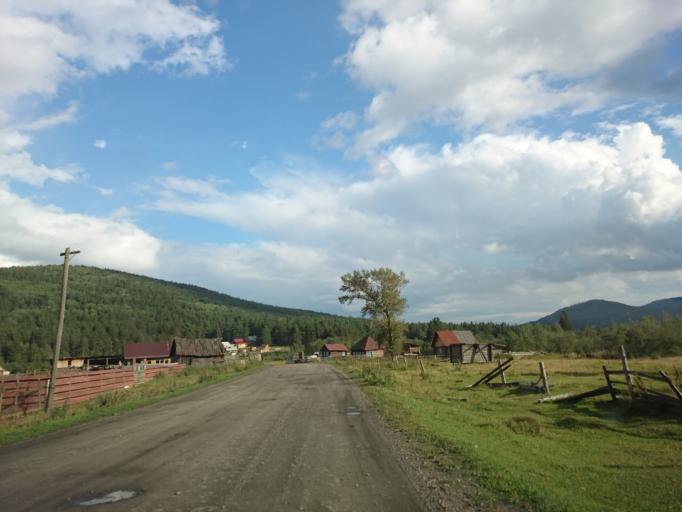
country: RU
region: Bashkortostan
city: Beloretsk
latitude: 54.0482
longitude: 58.3269
